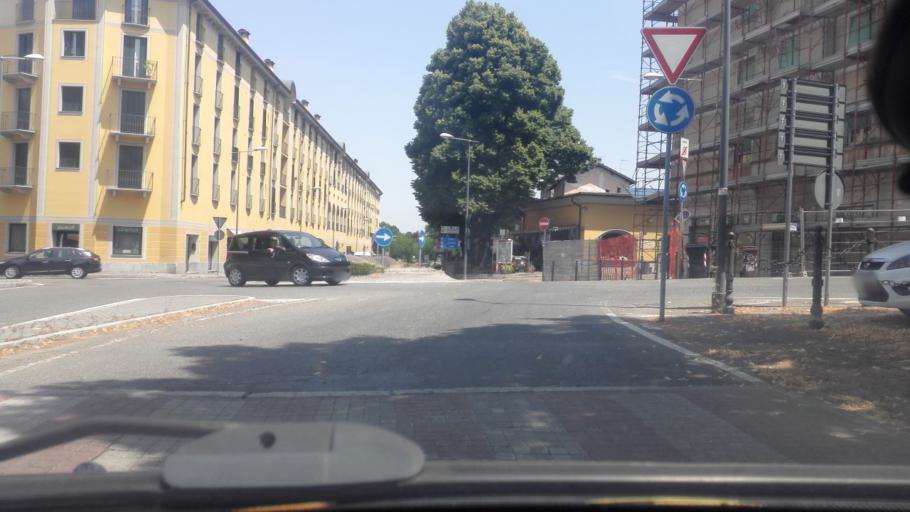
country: IT
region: Piedmont
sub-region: Provincia di Alessandria
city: Novi Ligure
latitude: 44.7611
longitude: 8.7808
